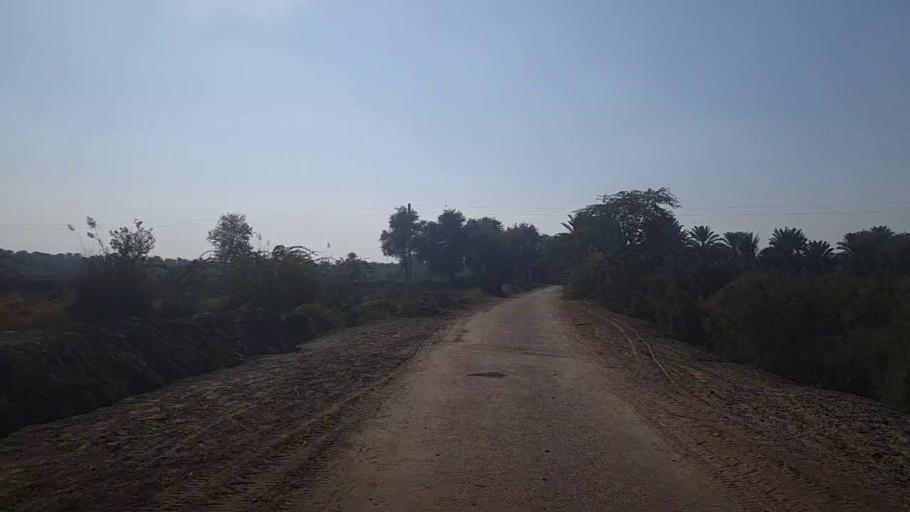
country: PK
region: Sindh
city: Khairpur
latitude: 27.4447
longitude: 68.7395
